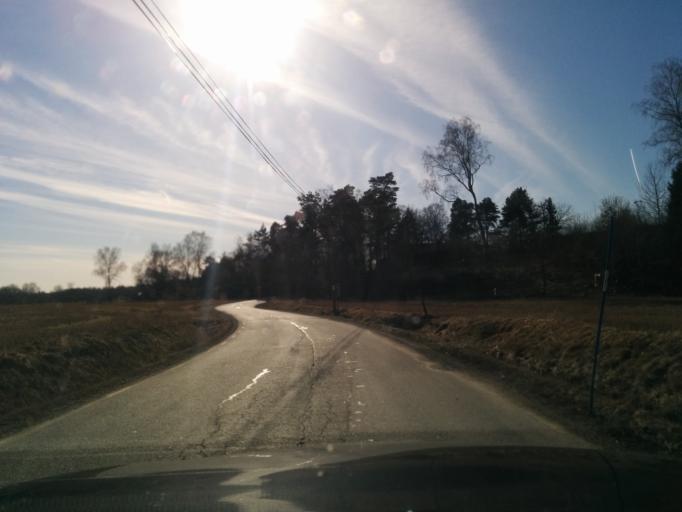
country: SE
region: Stockholm
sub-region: Vallentuna Kommun
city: Vallentuna
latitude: 59.5173
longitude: 18.0144
